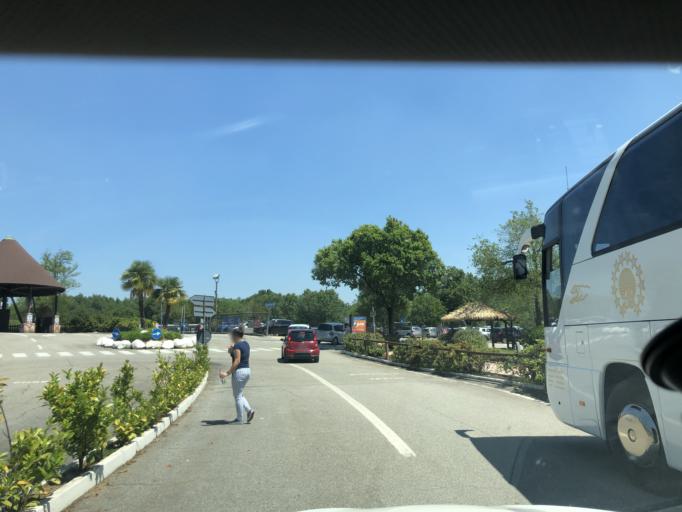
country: IT
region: Piedmont
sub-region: Provincia di Novara
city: Pombia
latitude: 45.6404
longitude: 8.6169
